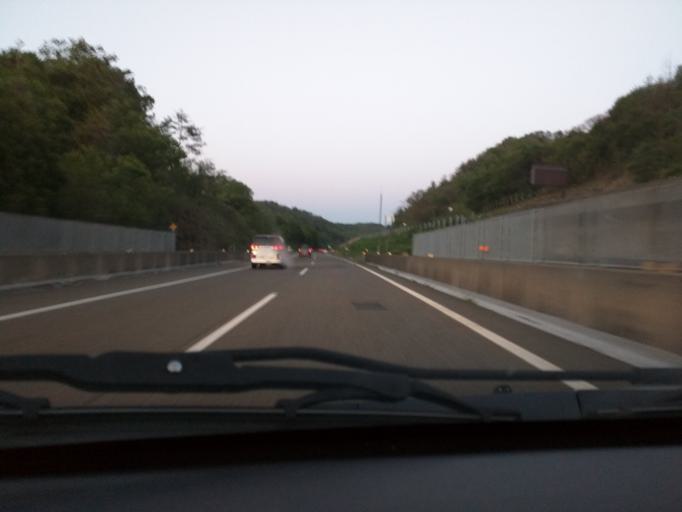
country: JP
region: Niigata
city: Kashiwazaki
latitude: 37.3397
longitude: 138.5230
